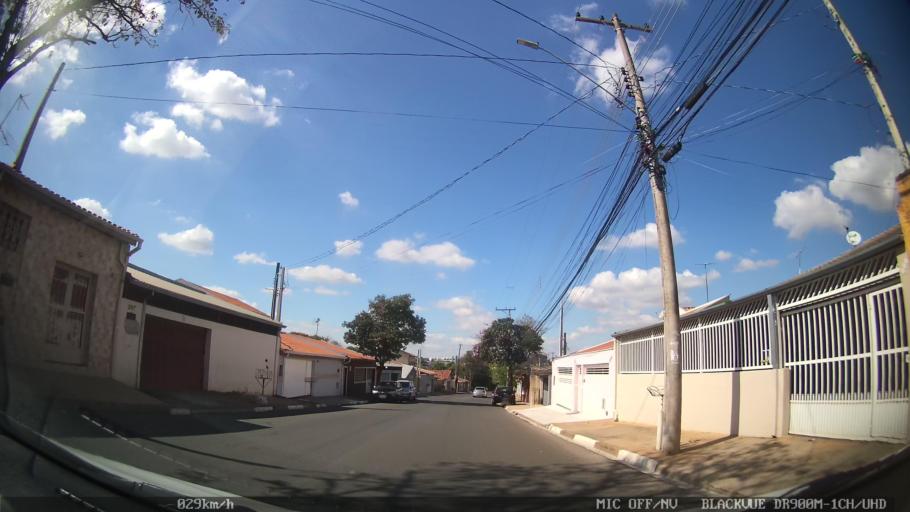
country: BR
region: Sao Paulo
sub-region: Hortolandia
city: Hortolandia
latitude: -22.8916
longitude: -47.2180
